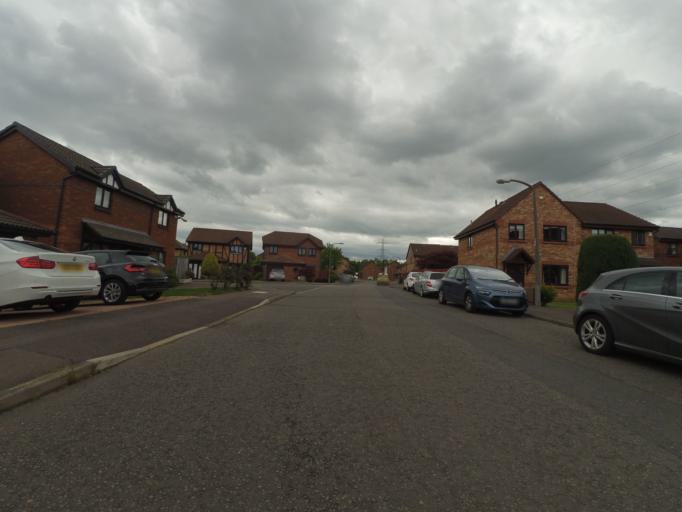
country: GB
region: Scotland
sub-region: East Lothian
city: Musselburgh
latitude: 55.9404
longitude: -3.0980
